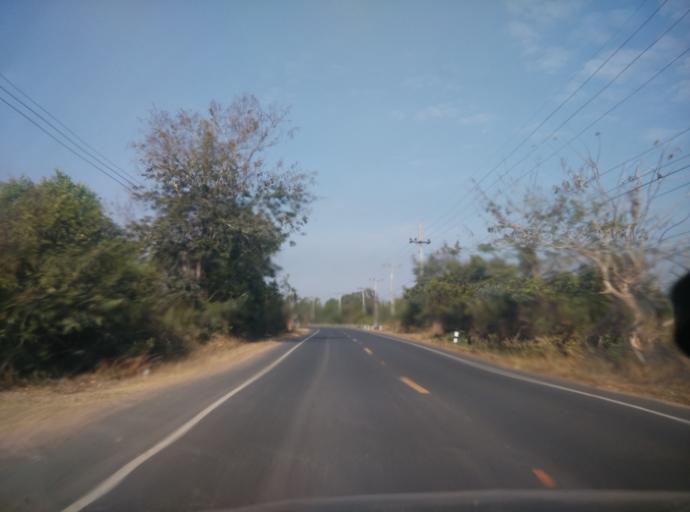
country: TH
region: Sisaket
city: Si Sa Ket
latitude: 15.1163
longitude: 104.2607
